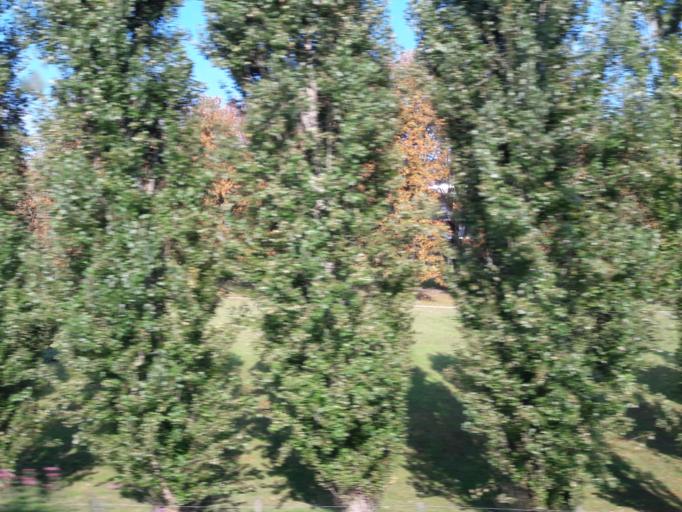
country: CH
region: Vaud
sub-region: Nyon District
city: Rolle
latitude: 46.4586
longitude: 6.3302
